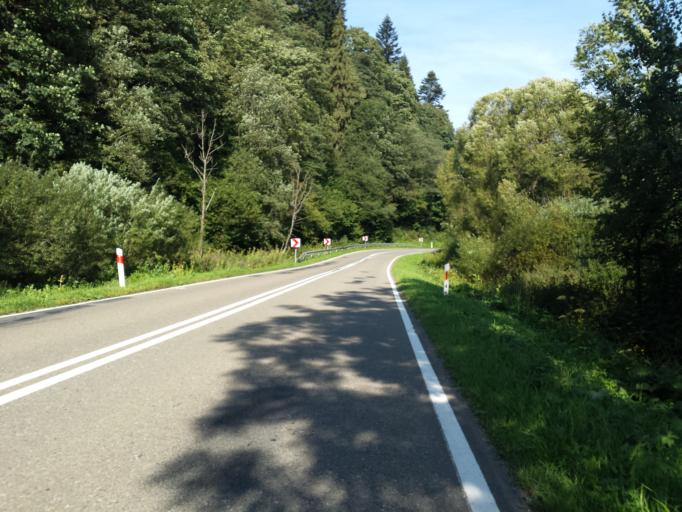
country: PL
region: Subcarpathian Voivodeship
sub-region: Powiat leski
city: Baligrod
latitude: 49.2841
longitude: 22.2770
